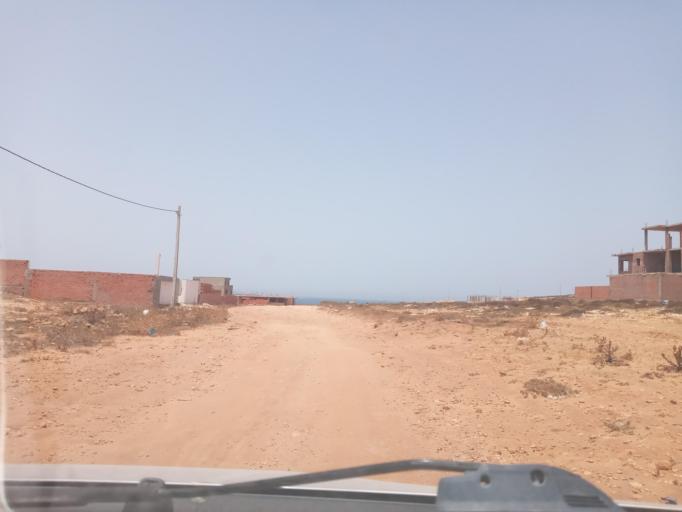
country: TN
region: Nabul
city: El Haouaria
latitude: 37.0534
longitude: 10.9999
